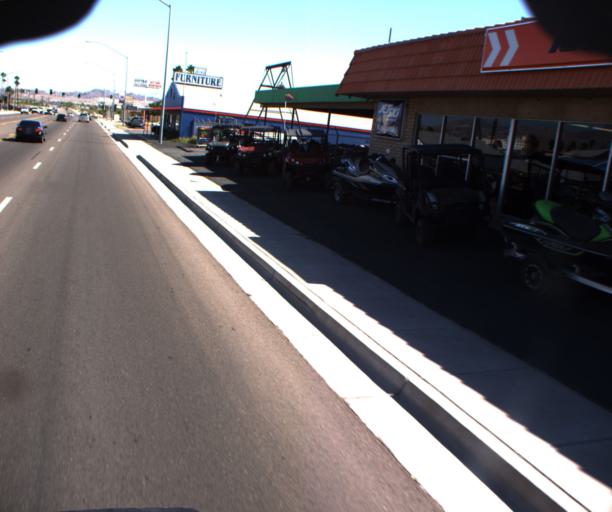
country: US
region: Arizona
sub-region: Mohave County
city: Bullhead City
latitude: 35.1515
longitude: -114.5677
